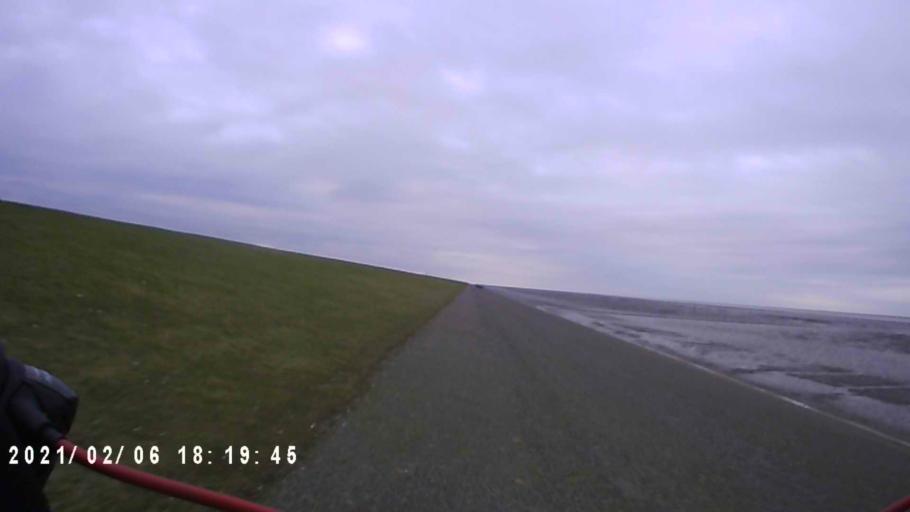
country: DE
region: Lower Saxony
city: Borkum
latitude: 53.4649
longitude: 6.7335
